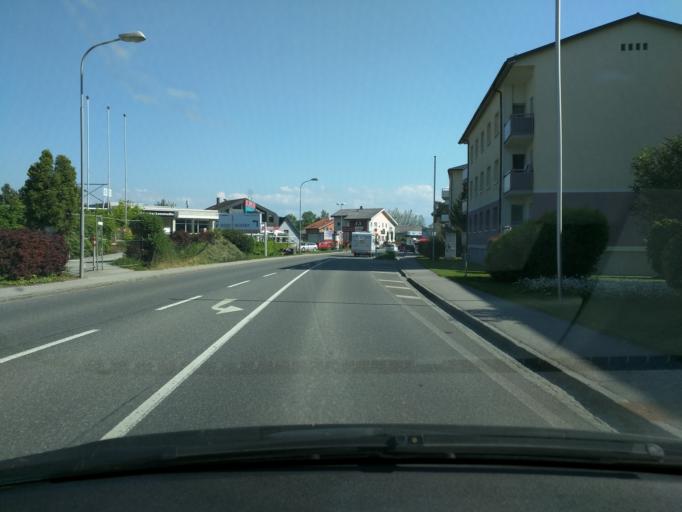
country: AT
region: Lower Austria
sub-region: Politischer Bezirk Melk
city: Ybbs an der Donau
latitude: 48.1755
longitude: 15.0835
